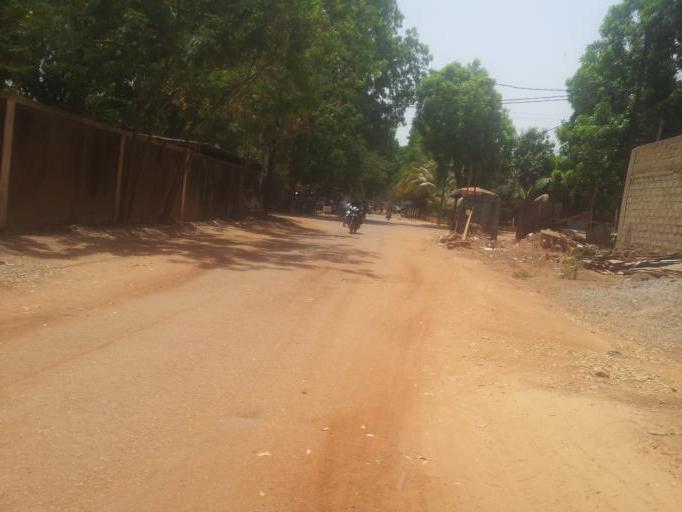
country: BF
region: Centre
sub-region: Kadiogo Province
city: Ouagadougou
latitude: 12.3740
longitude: -1.5133
